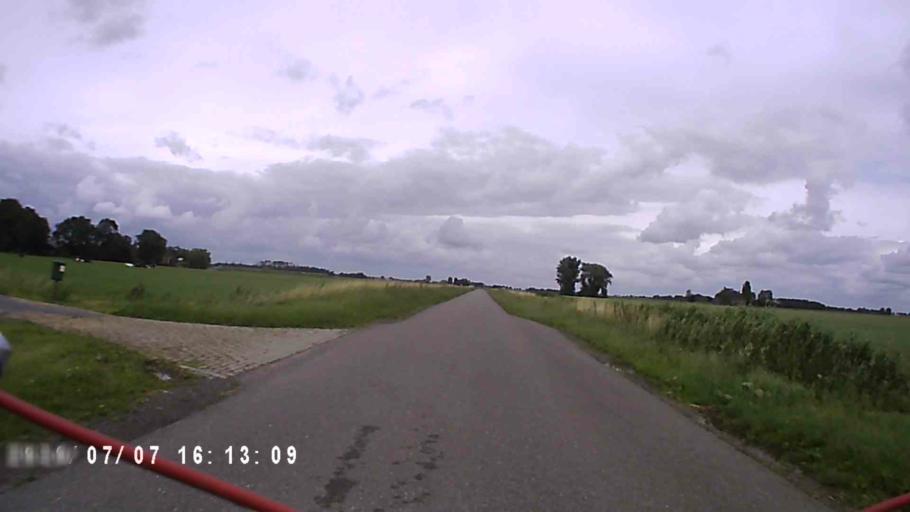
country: NL
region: Groningen
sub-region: Gemeente Winsum
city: Winsum
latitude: 53.3720
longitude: 6.5362
